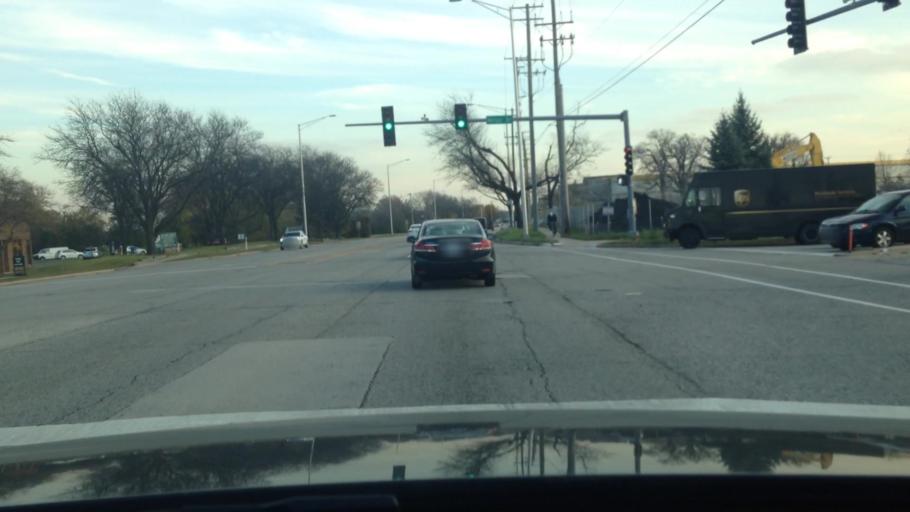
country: US
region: Illinois
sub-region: Cook County
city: Arlington Heights
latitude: 42.0500
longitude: -87.9921
